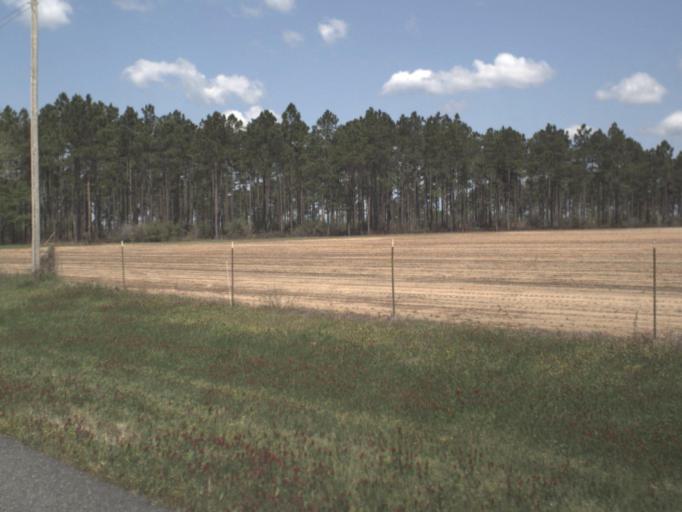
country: US
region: Alabama
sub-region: Escambia County
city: East Brewton
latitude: 30.9509
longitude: -87.0845
